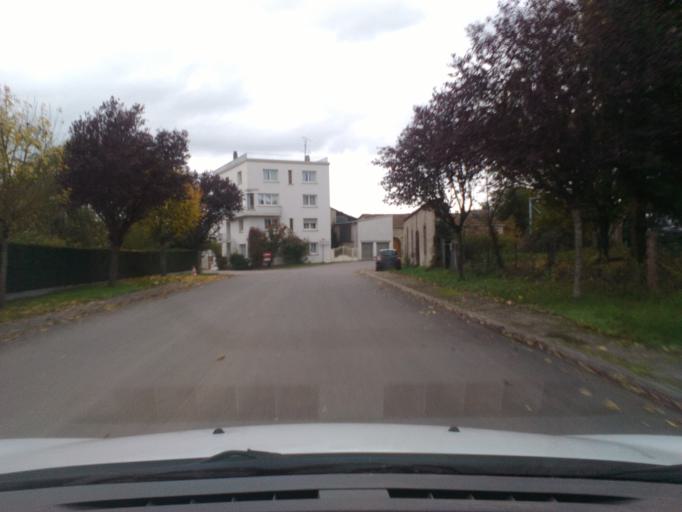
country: FR
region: Lorraine
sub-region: Departement des Vosges
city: Mirecourt
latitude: 48.3547
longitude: 6.0856
